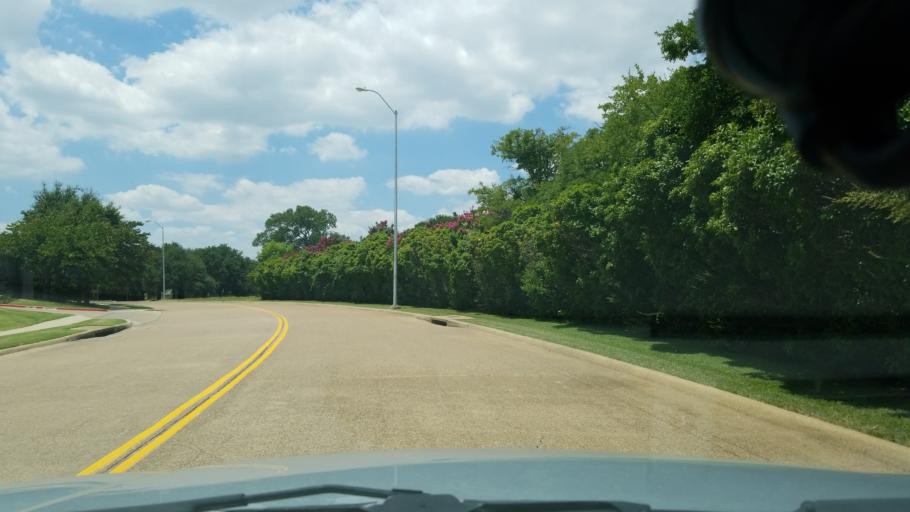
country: US
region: Texas
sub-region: Dallas County
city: Duncanville
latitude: 32.6833
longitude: -96.8809
